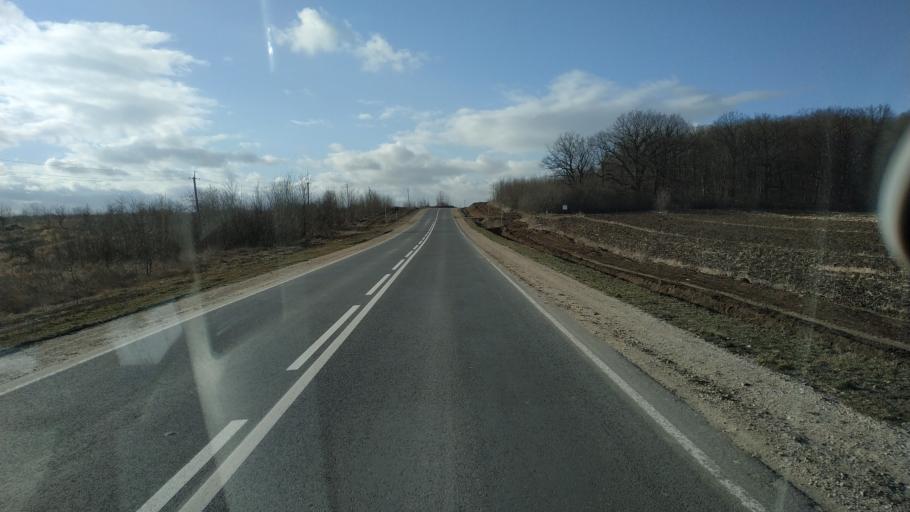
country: MD
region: Calarasi
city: Calarasi
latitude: 47.3066
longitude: 28.1328
